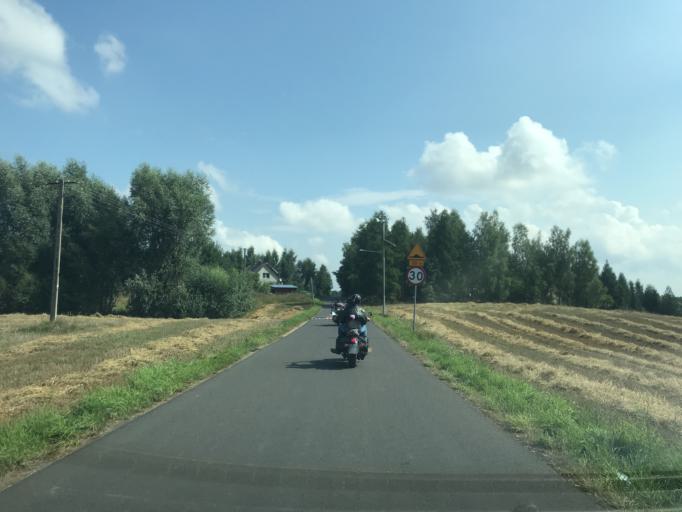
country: PL
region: Warmian-Masurian Voivodeship
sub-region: Powiat nowomiejski
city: Biskupiec
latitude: 53.4537
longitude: 19.4534
